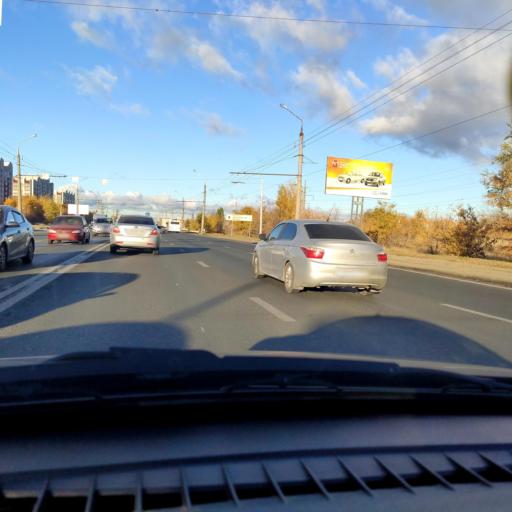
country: RU
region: Samara
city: Tol'yatti
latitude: 53.5500
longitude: 49.3304
